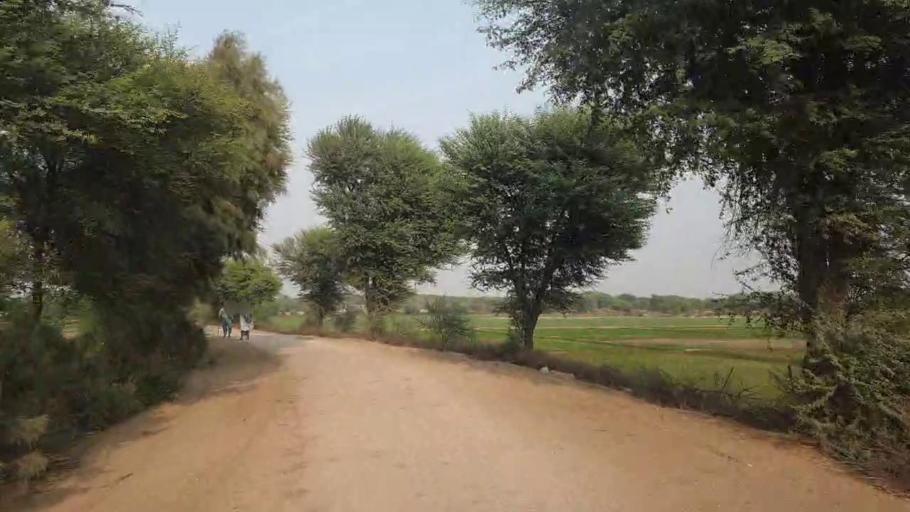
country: PK
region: Sindh
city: Sann
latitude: 26.1251
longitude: 68.0630
